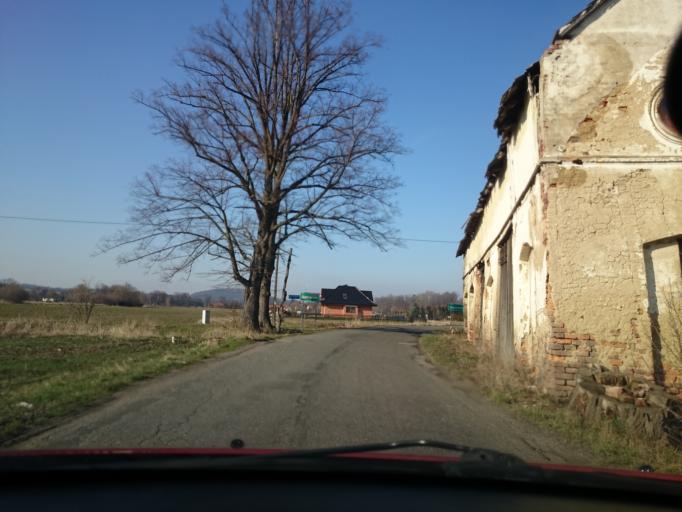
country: PL
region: Lower Silesian Voivodeship
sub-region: Powiat klodzki
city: Klodzko
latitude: 50.3711
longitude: 16.6365
